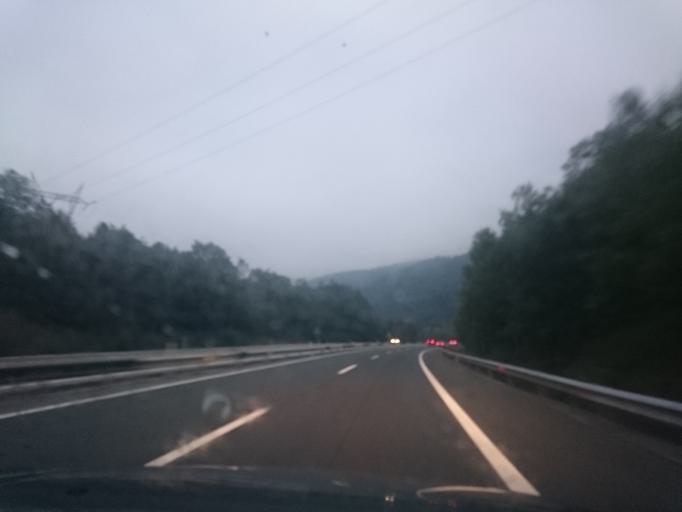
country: ES
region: Asturias
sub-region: Province of Asturias
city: Pola de Lena
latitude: 43.0368
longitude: -5.8230
